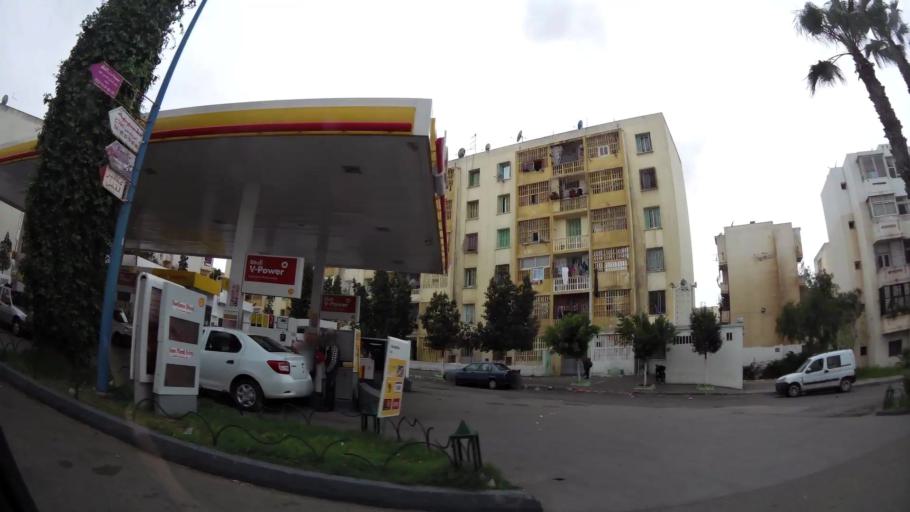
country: MA
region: Grand Casablanca
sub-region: Casablanca
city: Casablanca
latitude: 33.5740
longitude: -7.5541
